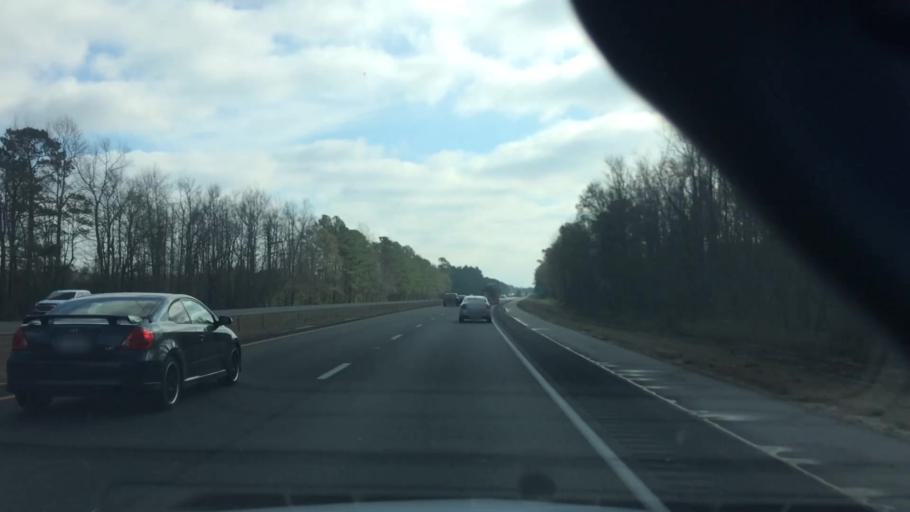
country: US
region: North Carolina
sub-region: Pender County
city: Burgaw
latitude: 34.6078
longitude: -77.9171
